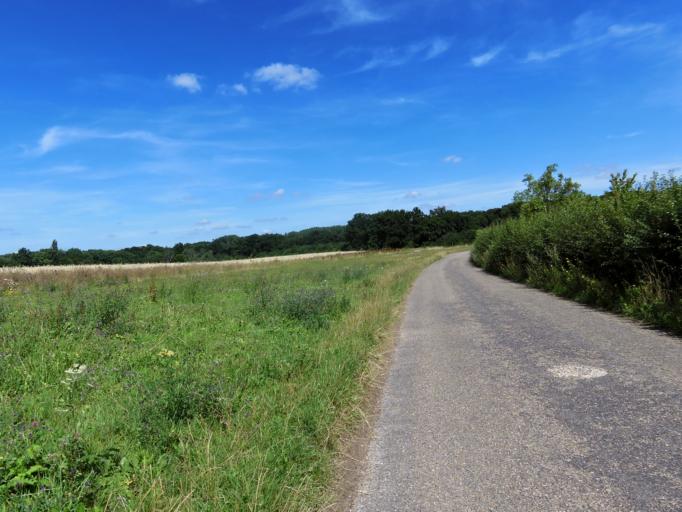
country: NL
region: Limburg
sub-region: Gemeente Voerendaal
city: Kunrade
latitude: 50.8847
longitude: 5.9554
